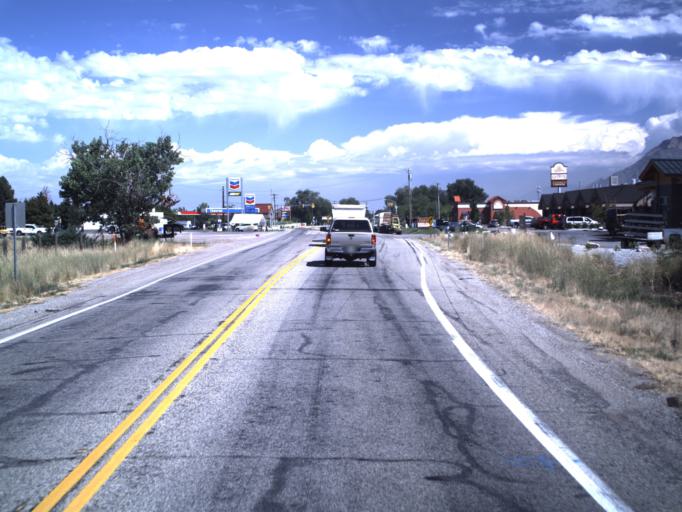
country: US
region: Utah
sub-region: Weber County
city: Marriott-Slaterville
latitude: 41.2664
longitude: -112.0273
